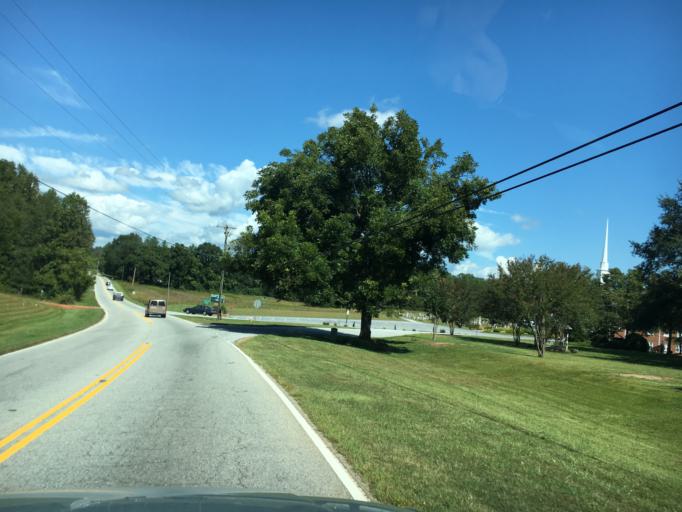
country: US
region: South Carolina
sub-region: Greenville County
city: Taylors
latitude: 34.9797
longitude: -82.3322
